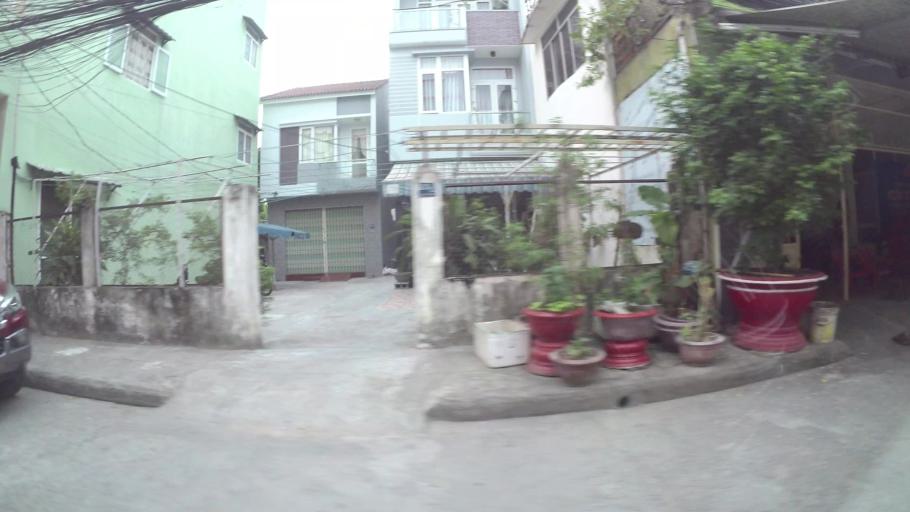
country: VN
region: Da Nang
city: Da Nang
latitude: 16.0740
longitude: 108.2214
